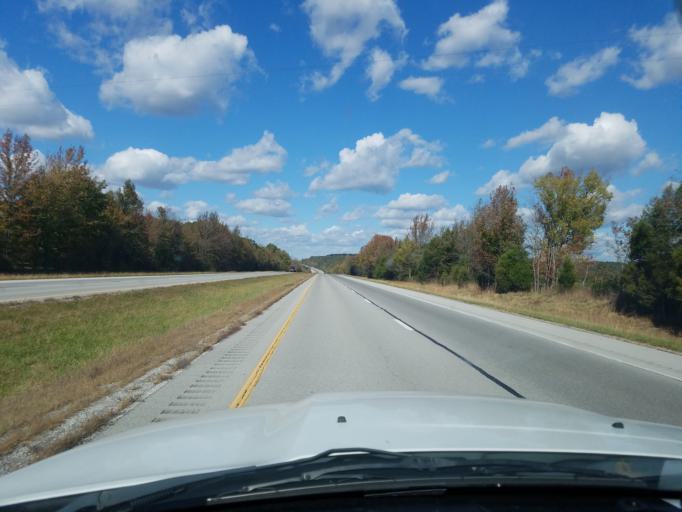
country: US
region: Kentucky
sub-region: Butler County
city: Morgantown
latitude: 37.0802
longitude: -86.6176
